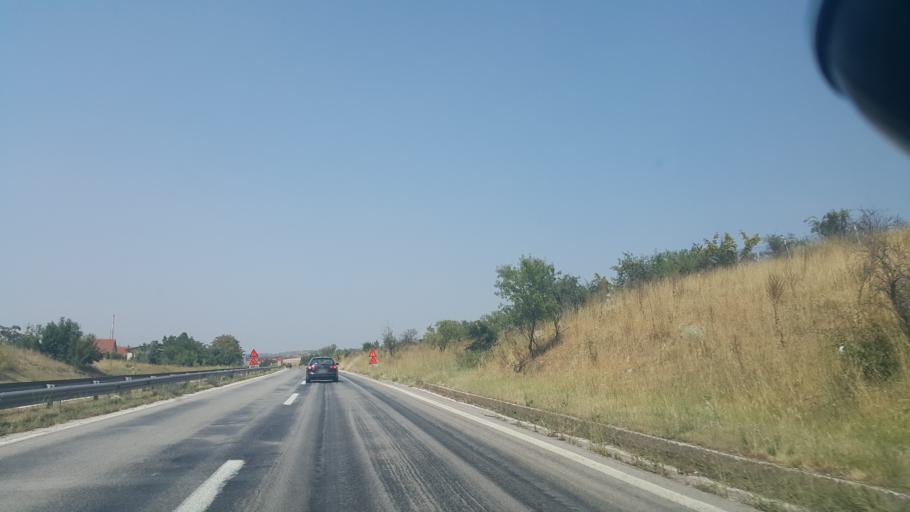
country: MK
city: Miladinovci
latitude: 41.9757
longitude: 21.6504
